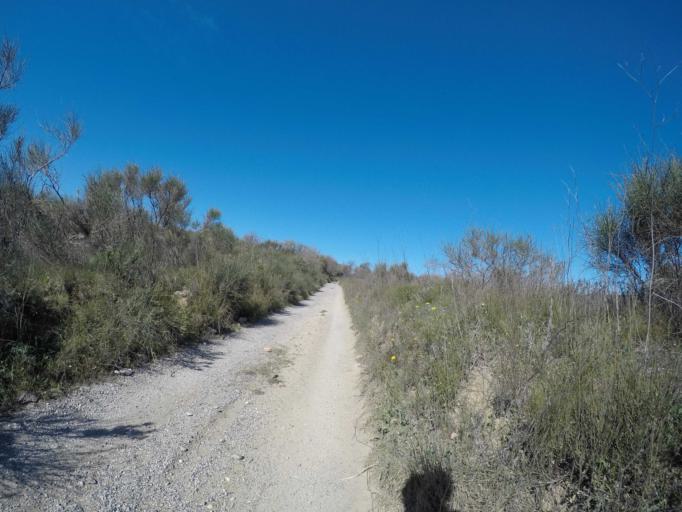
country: FR
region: Languedoc-Roussillon
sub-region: Departement des Pyrenees-Orientales
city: Millas
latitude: 42.7047
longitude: 2.6764
